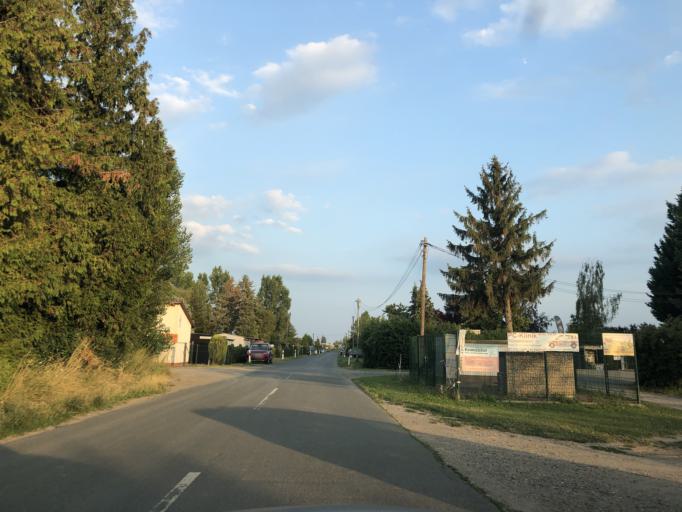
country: DE
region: Rheinland-Pfalz
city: Oppenheim
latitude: 49.8773
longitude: 8.3806
